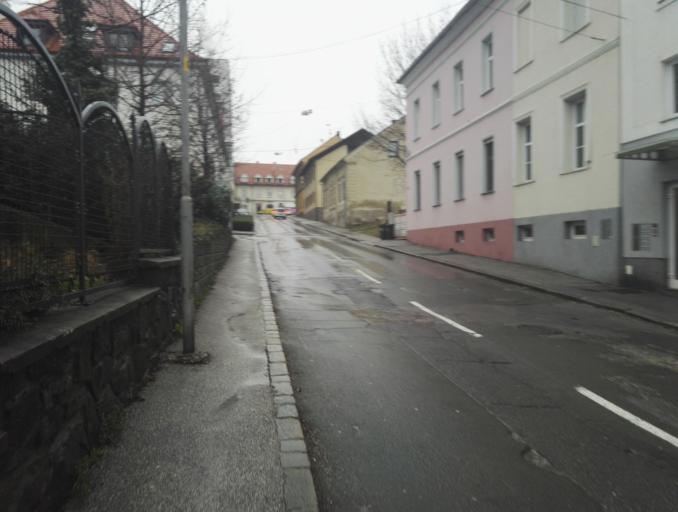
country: SI
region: Maribor
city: Maribor
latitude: 46.5578
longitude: 15.6364
